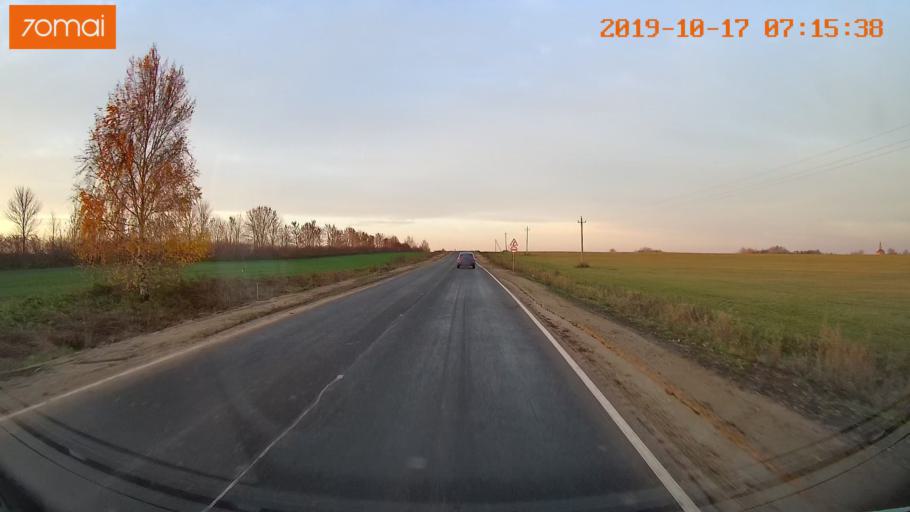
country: RU
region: Vladimir
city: Suzdal'
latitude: 56.3788
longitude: 40.2642
